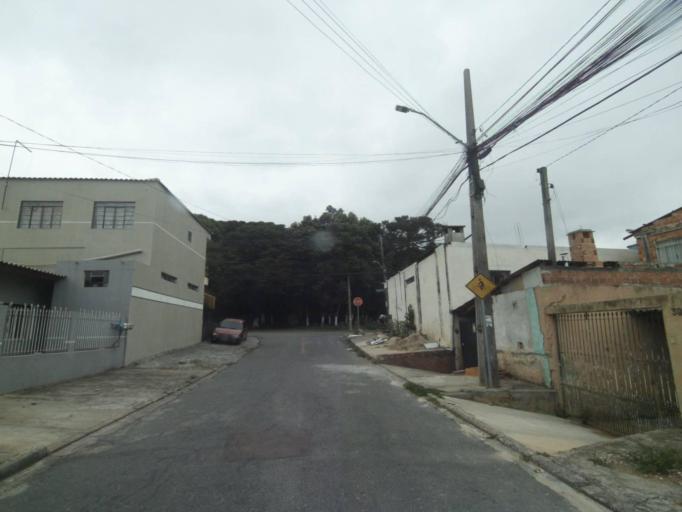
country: BR
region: Parana
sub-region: Araucaria
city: Araucaria
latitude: -25.5334
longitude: -49.3346
